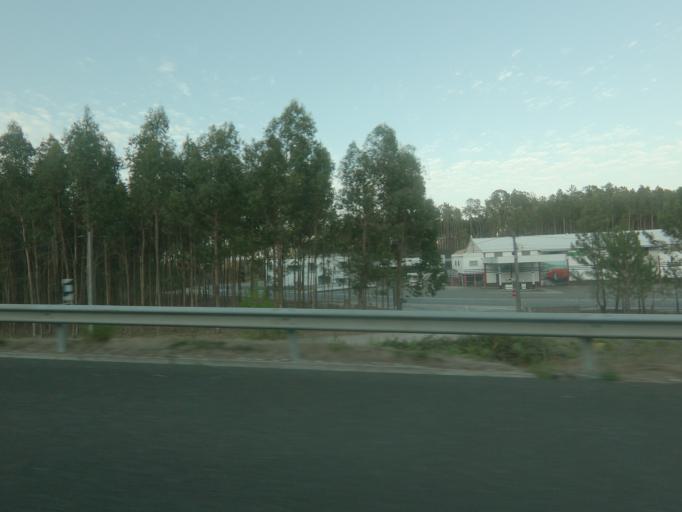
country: PT
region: Leiria
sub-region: Leiria
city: Caranguejeira
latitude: 39.7212
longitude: -8.7145
